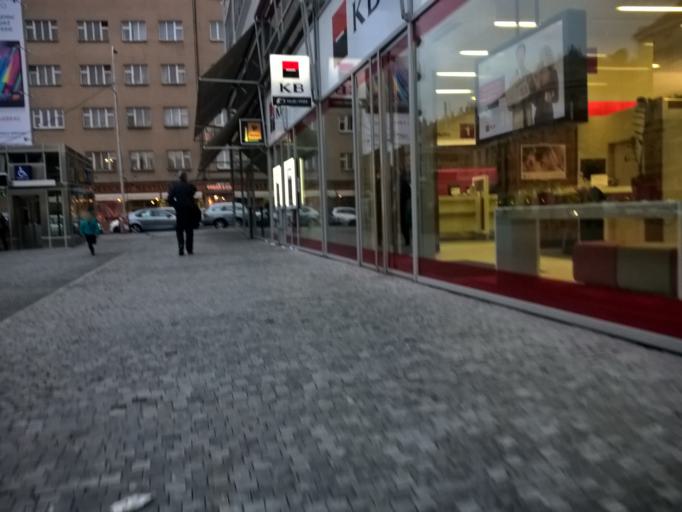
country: CZ
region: Praha
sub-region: Praha 2
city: Vysehrad
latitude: 50.0707
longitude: 14.4044
